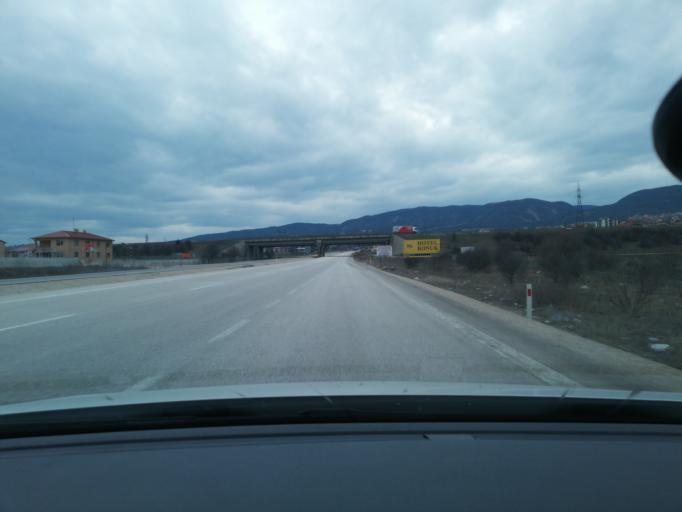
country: TR
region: Bolu
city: Gerede
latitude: 40.7793
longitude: 32.2159
